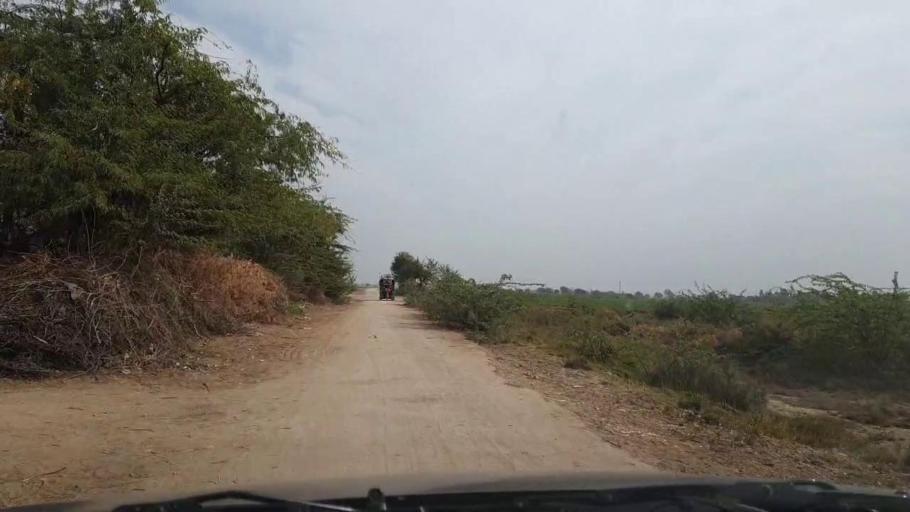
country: PK
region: Sindh
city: Sinjhoro
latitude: 26.0648
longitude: 68.8434
